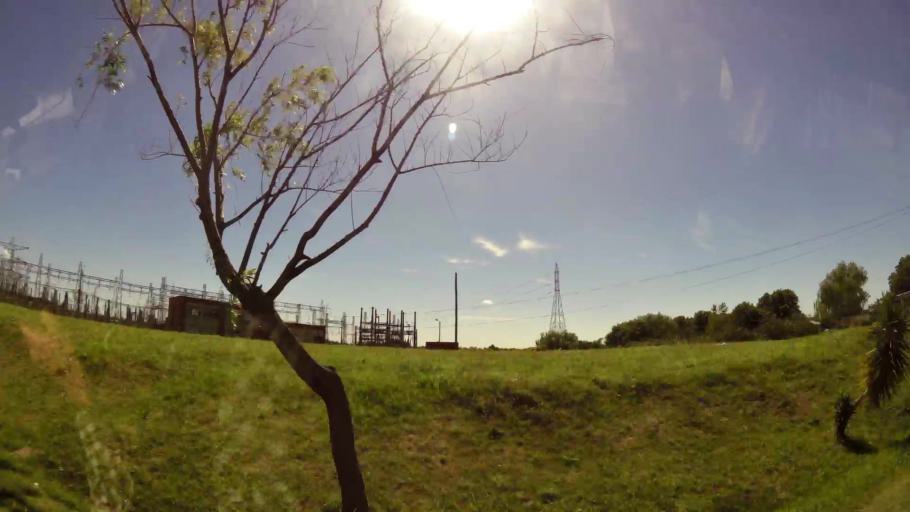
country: UY
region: Canelones
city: Paso de Carrasco
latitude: -34.8626
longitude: -56.1117
